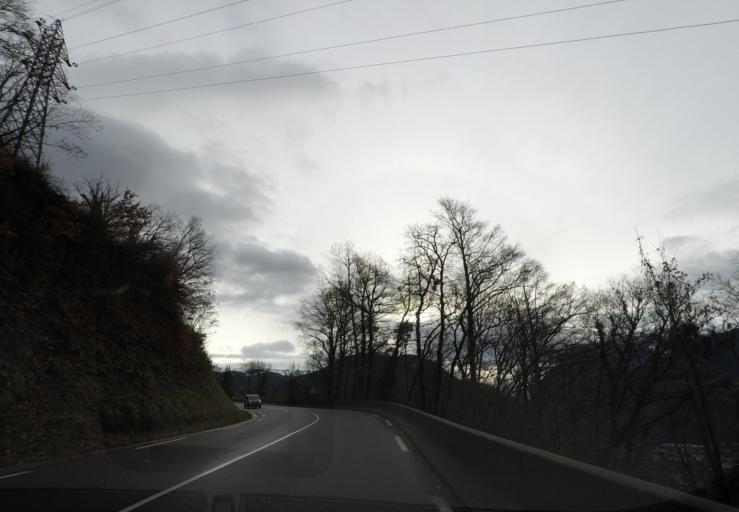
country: FR
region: Rhone-Alpes
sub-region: Departement de la Haute-Savoie
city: Chatillon-sur-Cluses
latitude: 46.0844
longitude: 6.5734
